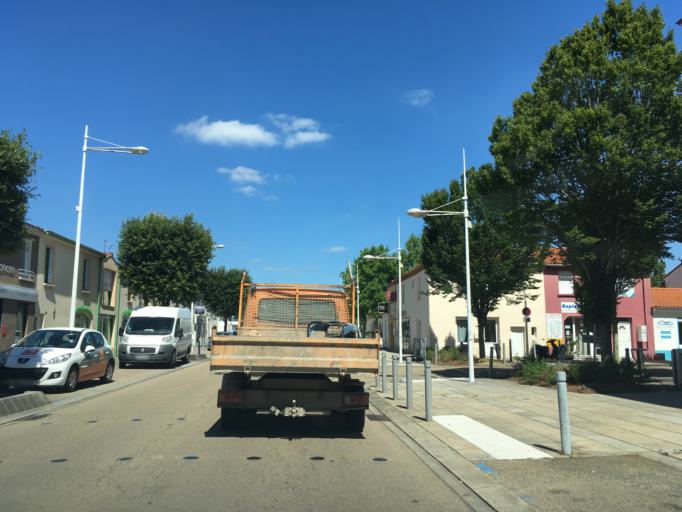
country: FR
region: Pays de la Loire
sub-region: Departement de la Loire-Atlantique
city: Les Sorinieres
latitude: 47.1478
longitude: -1.5305
